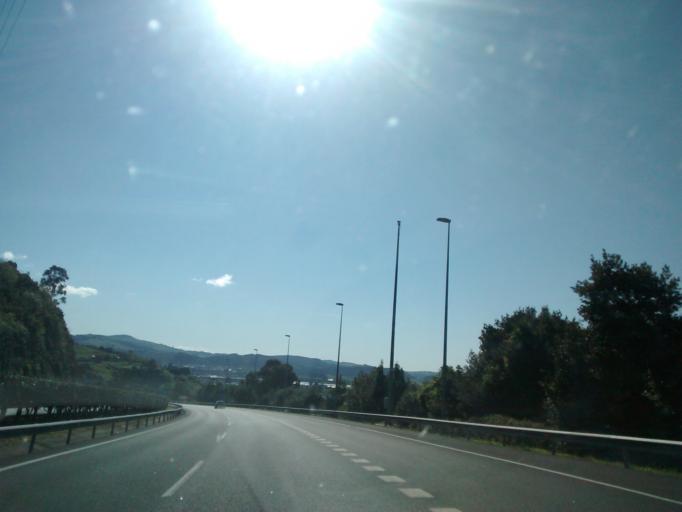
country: ES
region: Cantabria
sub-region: Provincia de Cantabria
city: Laredo
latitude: 43.4048
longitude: -3.4144
